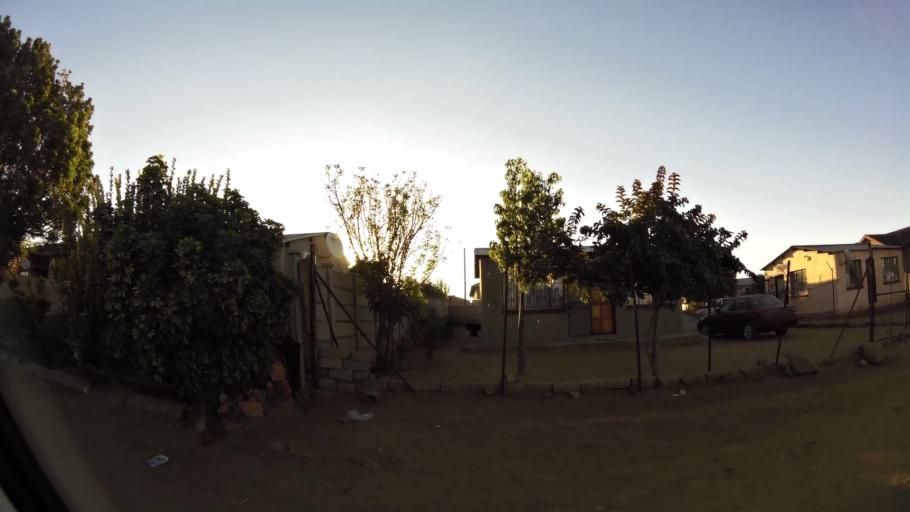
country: ZA
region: Limpopo
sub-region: Capricorn District Municipality
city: Polokwane
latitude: -23.8482
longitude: 29.3511
